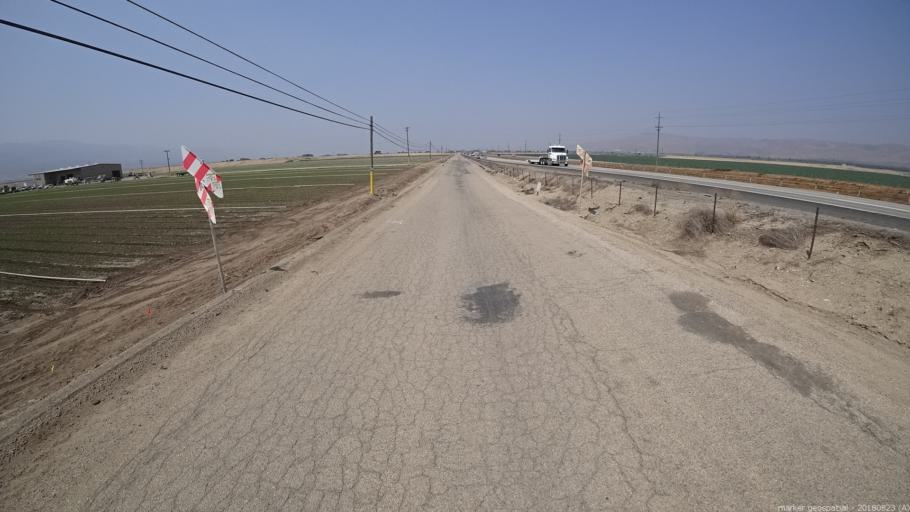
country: US
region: California
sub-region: Monterey County
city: Soledad
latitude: 36.3879
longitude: -121.3058
